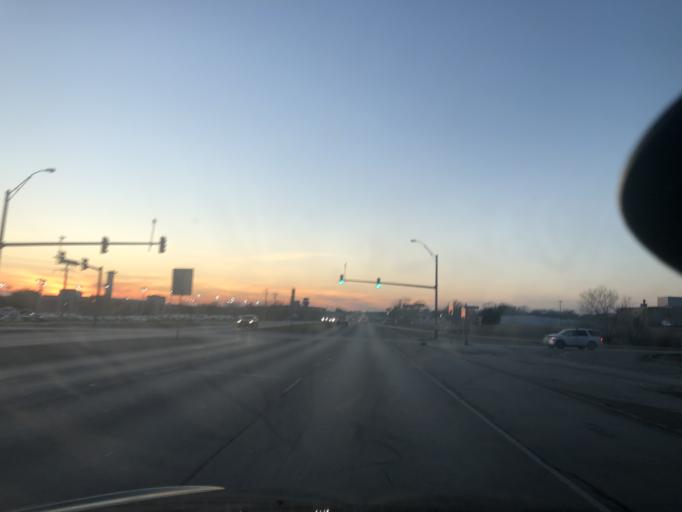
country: US
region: Texas
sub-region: Tarrant County
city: White Settlement
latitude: 32.7247
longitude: -97.4809
